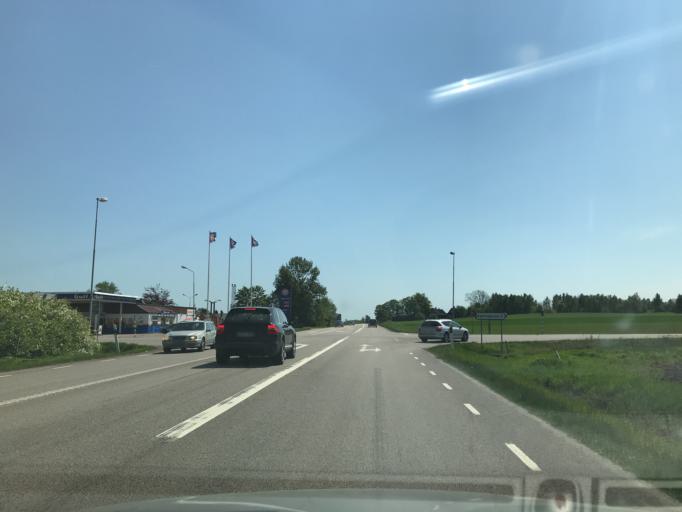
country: SE
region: Skane
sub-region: Astorps Kommun
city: Kvidinge
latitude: 56.1875
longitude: 13.0559
